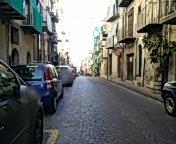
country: IT
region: Sicily
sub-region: Palermo
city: Castelbuono
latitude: 37.9289
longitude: 14.0899
